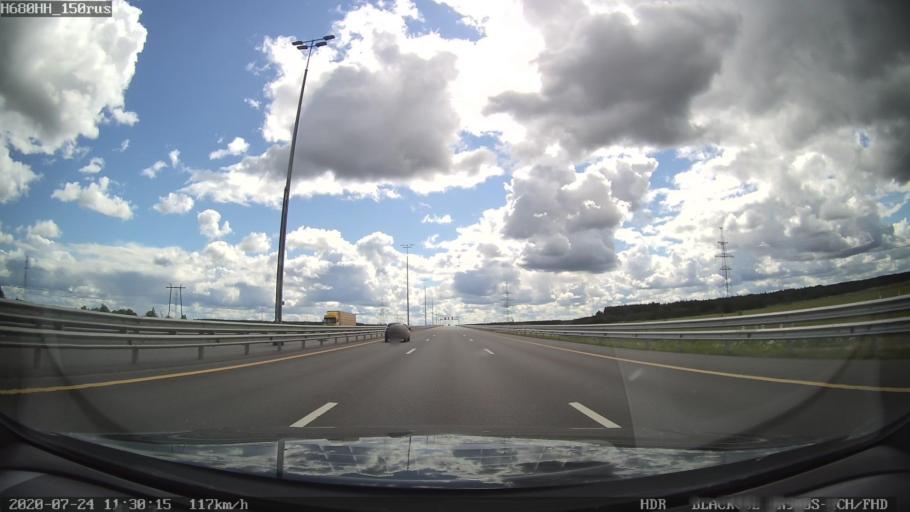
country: RU
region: Leningrad
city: Krasnyy Bor
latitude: 59.6713
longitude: 30.6091
